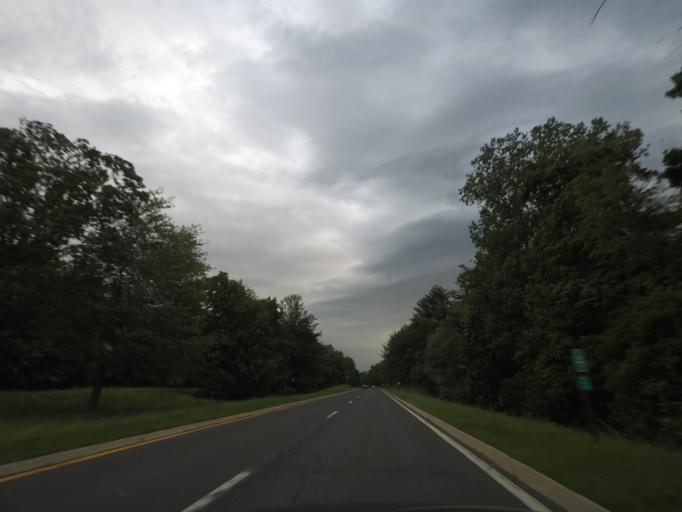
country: US
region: New York
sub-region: Columbia County
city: Philmont
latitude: 42.2348
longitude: -73.6248
